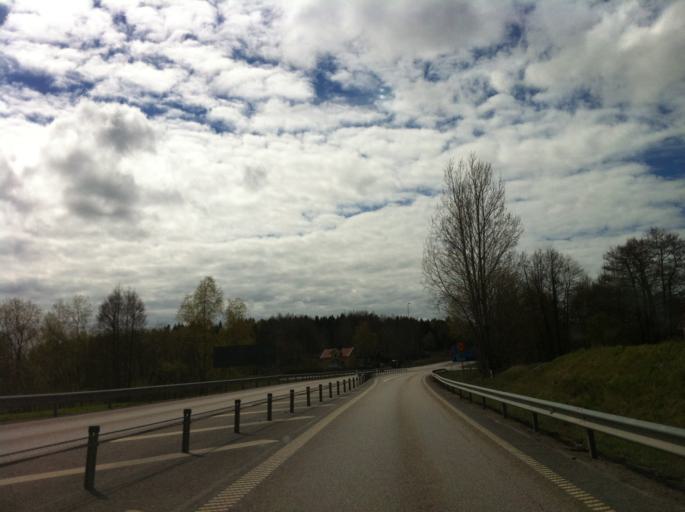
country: SE
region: OEstergoetland
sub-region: Valdemarsviks Kommun
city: Valdemarsvik
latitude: 58.1437
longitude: 16.5348
